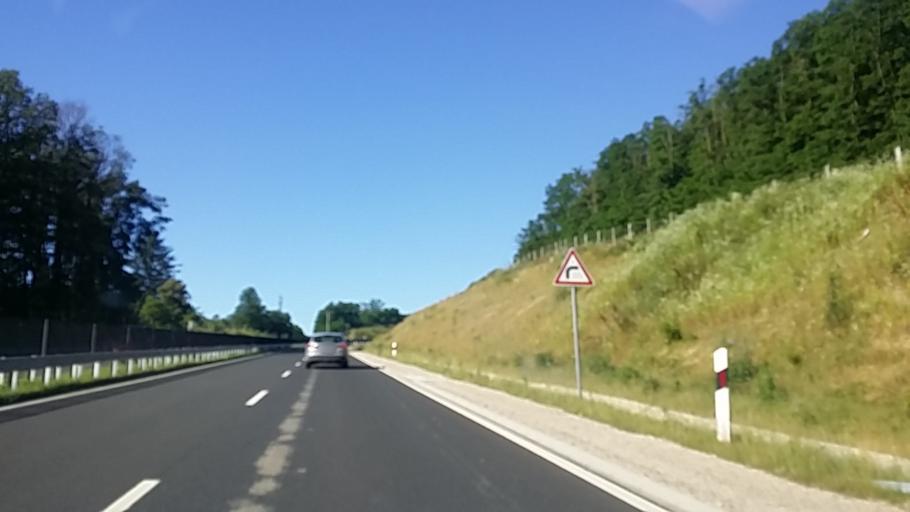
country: HU
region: Zala
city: Heviz
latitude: 46.7911
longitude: 17.1392
